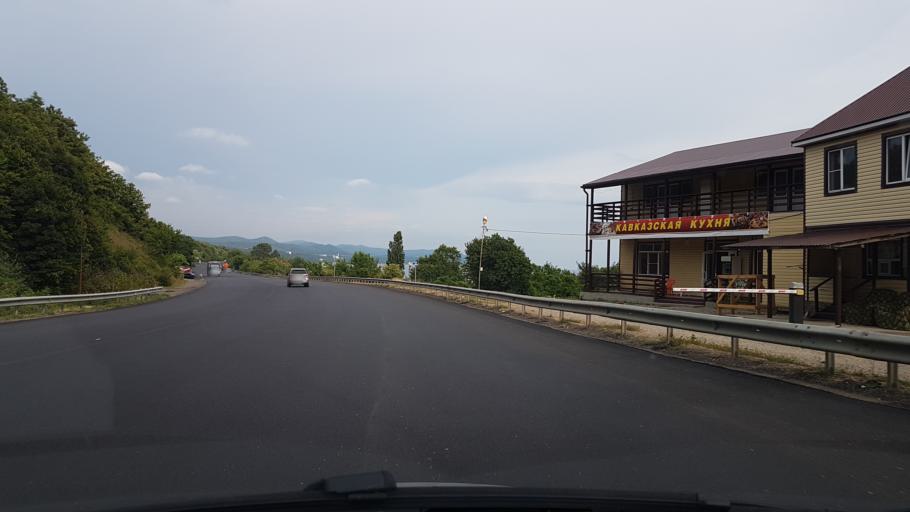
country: RU
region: Krasnodarskiy
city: Lermontovo
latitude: 44.2944
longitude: 38.7599
